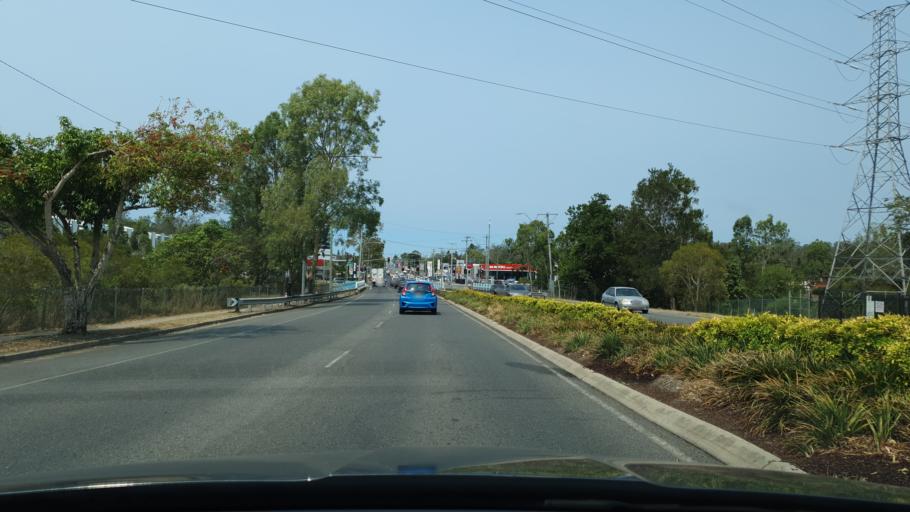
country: AU
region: Queensland
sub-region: Ipswich
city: Bundamba
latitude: -27.6109
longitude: 152.8051
